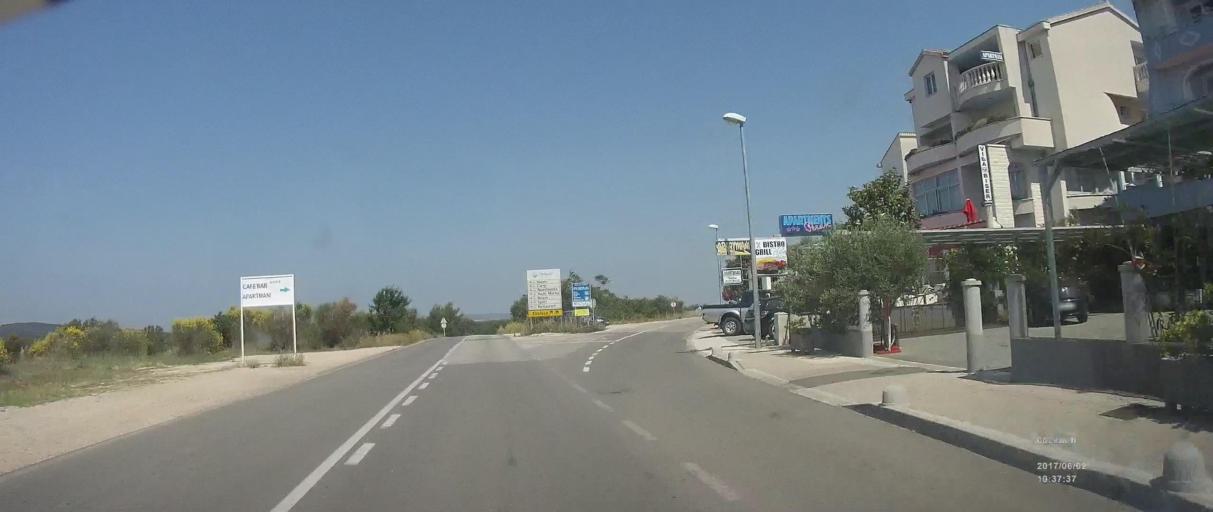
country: HR
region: Sibensko-Kniniska
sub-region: Grad Sibenik
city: Sibenik
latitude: 43.7010
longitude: 15.8962
